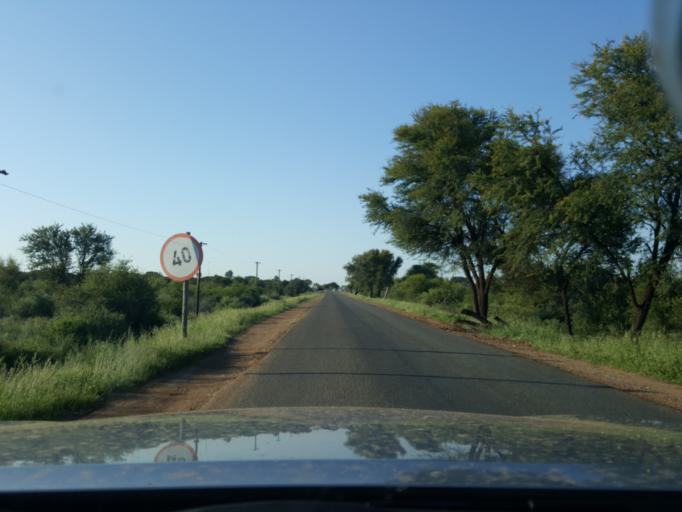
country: ZA
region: North-West
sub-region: Ngaka Modiri Molema District Municipality
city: Mmabatho
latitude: -25.6423
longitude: 25.5741
